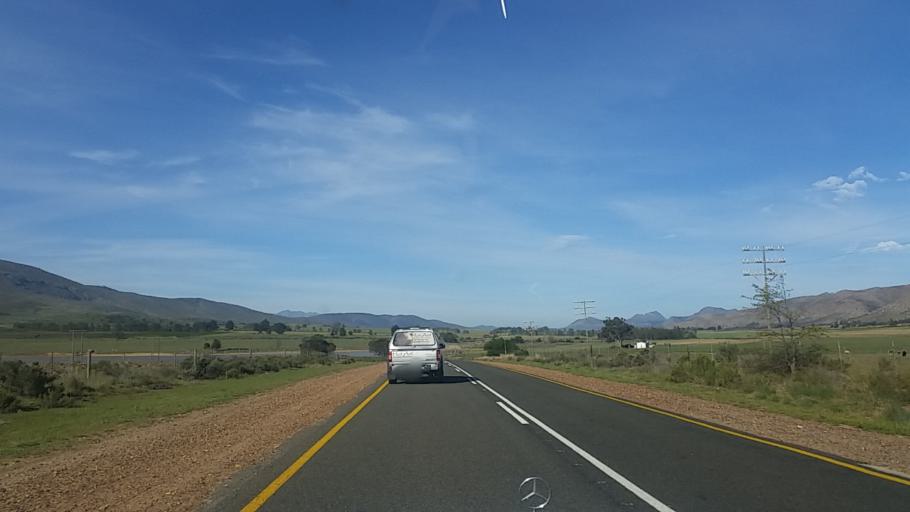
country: ZA
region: Western Cape
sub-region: Eden District Municipality
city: George
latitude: -33.8327
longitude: 22.4547
